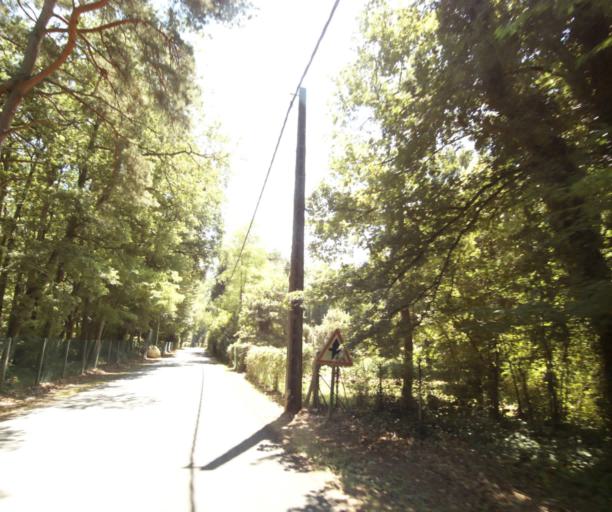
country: FR
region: Centre
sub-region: Departement du Loiret
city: Malesherbes
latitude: 48.2961
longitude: 2.4262
